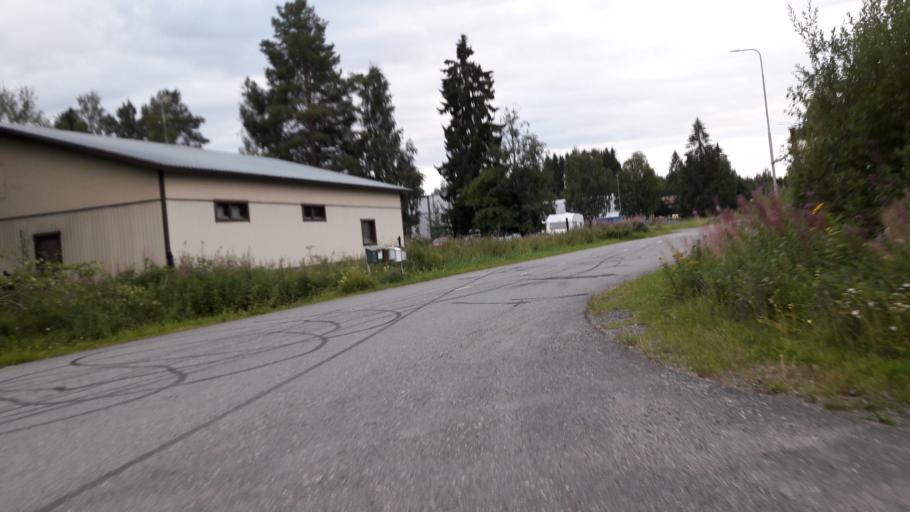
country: FI
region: North Karelia
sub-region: Joensuu
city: Joensuu
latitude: 62.5516
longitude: 29.8345
